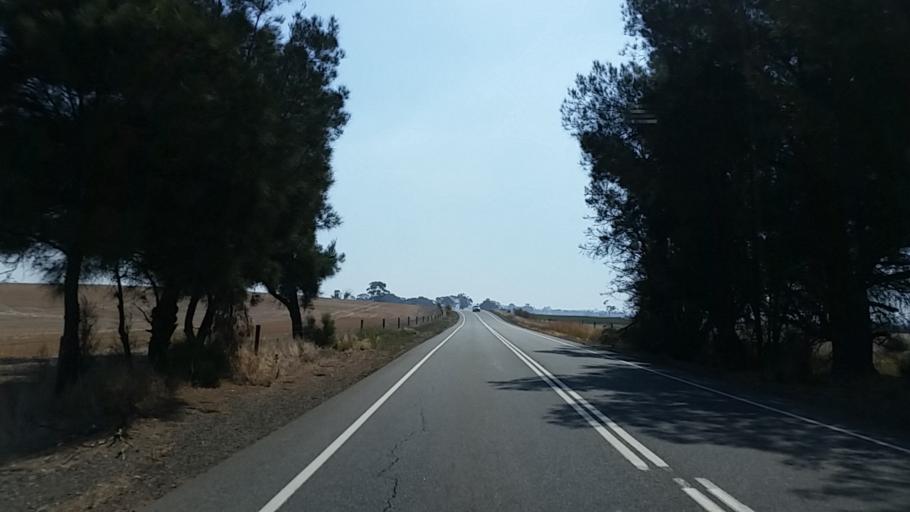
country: AU
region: South Australia
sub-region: Light
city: Kapunda
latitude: -34.2559
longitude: 138.7543
